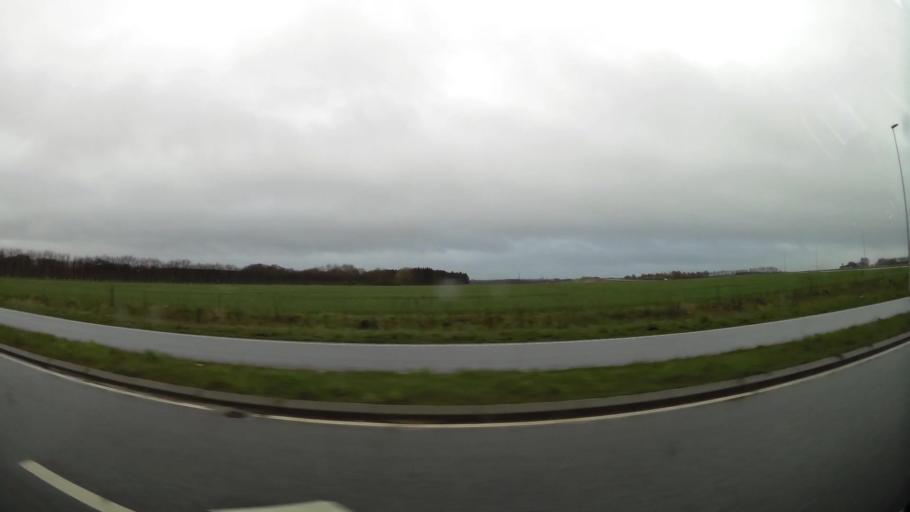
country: DK
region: Central Jutland
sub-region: Herning Kommune
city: Snejbjerg
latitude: 56.1534
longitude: 8.8934
